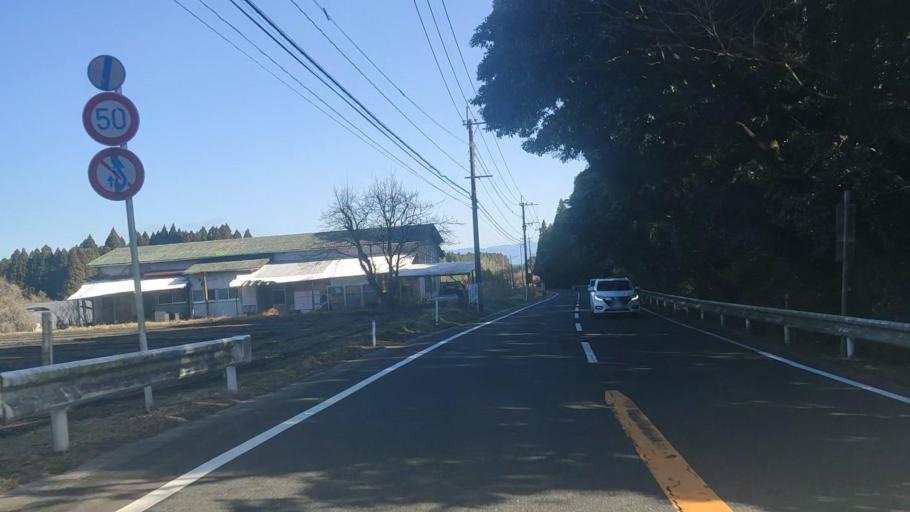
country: JP
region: Kagoshima
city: Sueyoshicho-ninokata
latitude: 31.6864
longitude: 130.9463
